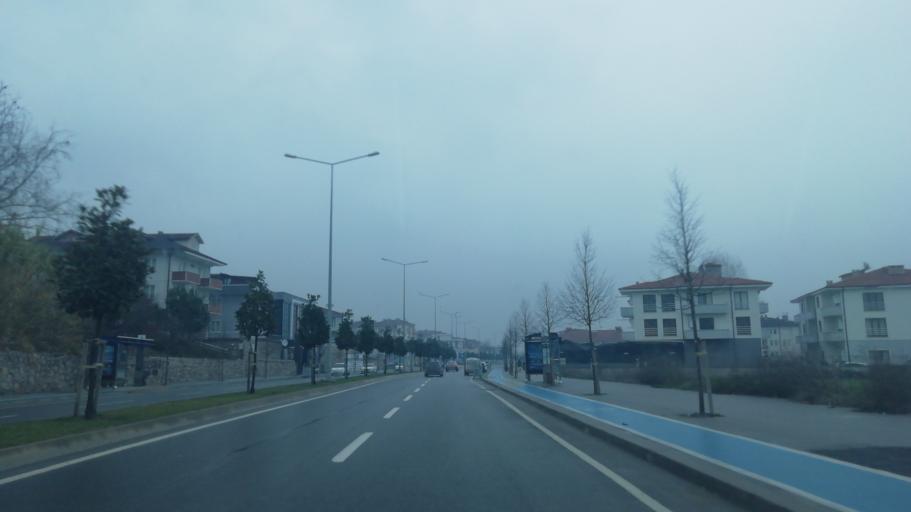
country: TR
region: Sakarya
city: Adapazari
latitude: 40.7594
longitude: 30.3547
